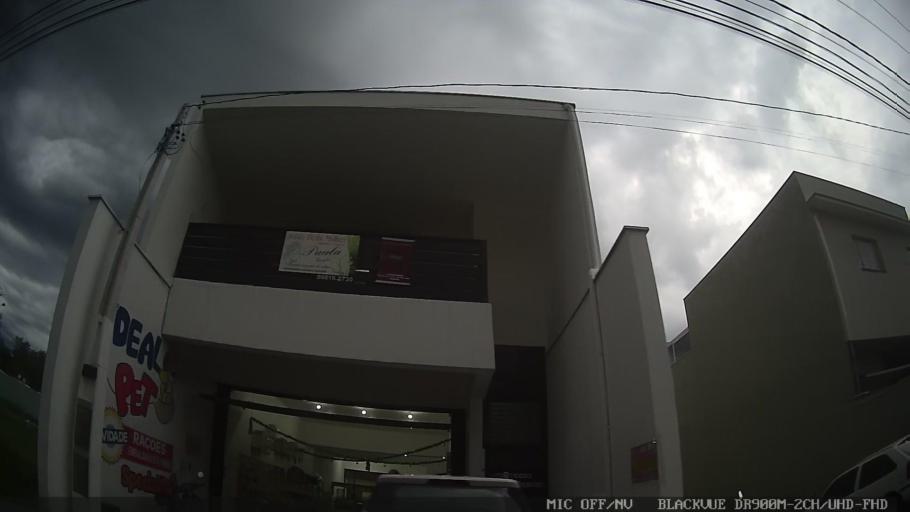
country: BR
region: Sao Paulo
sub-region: Amparo
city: Amparo
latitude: -22.7147
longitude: -46.7994
